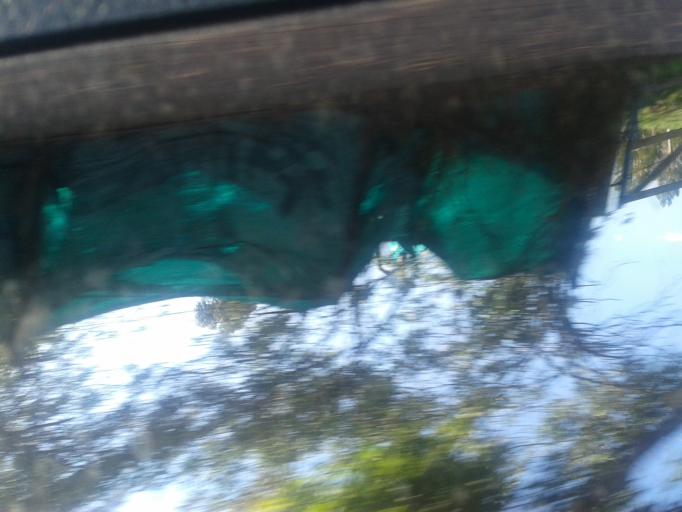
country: CO
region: Bogota D.C.
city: Barrio San Luis
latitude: 4.7225
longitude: -74.0623
